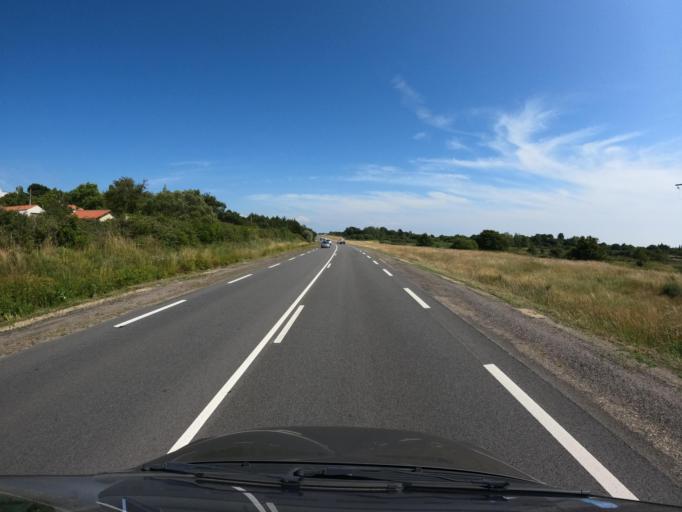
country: FR
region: Pays de la Loire
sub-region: Departement de la Loire-Atlantique
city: Les Moutiers-en-Retz
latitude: 47.0600
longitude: -1.9782
